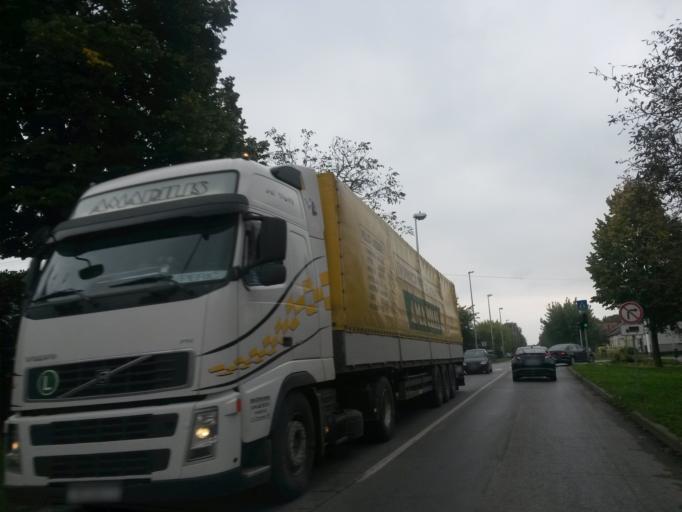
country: HR
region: Osjecko-Baranjska
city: Piskorevci
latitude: 45.3096
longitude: 18.4163
